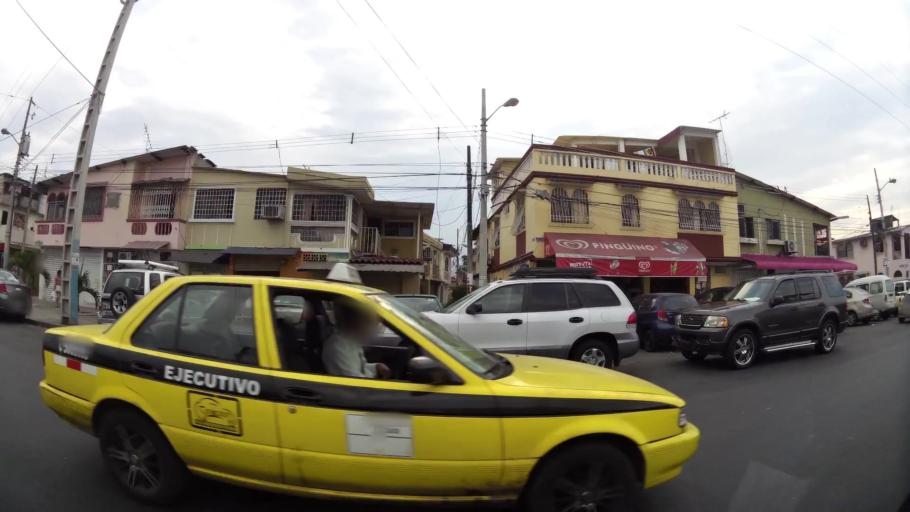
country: EC
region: Guayas
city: Guayaquil
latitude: -2.2411
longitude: -79.8874
